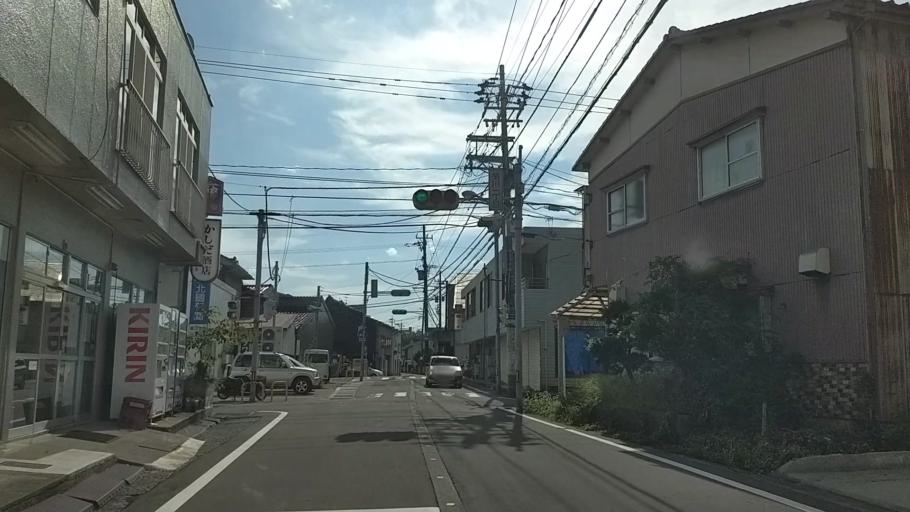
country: JP
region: Ishikawa
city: Nonoichi
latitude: 36.5502
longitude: 136.6646
